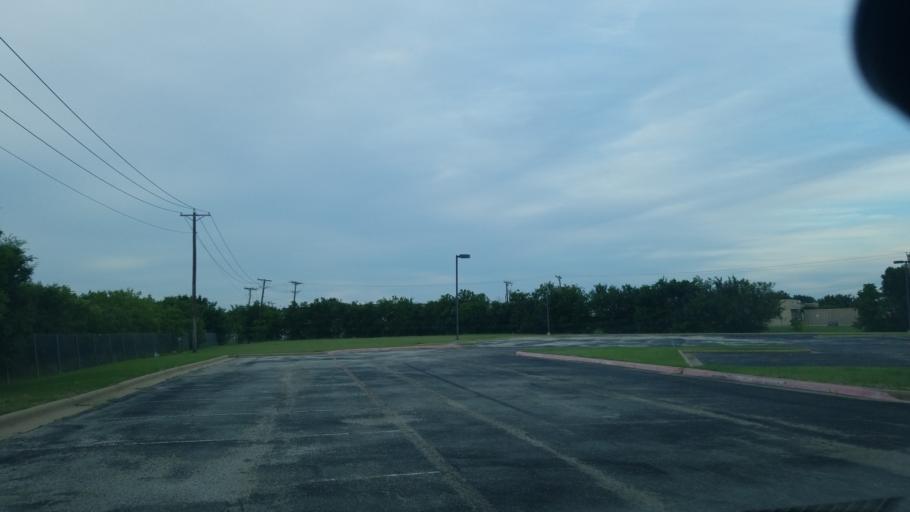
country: US
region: Texas
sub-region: Dallas County
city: Irving
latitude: 32.8739
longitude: -96.9783
